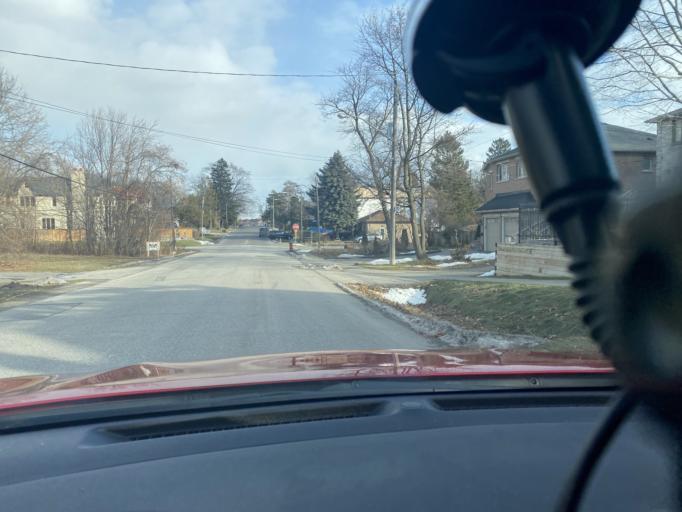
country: CA
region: Ontario
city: Scarborough
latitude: 43.7950
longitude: -79.1692
